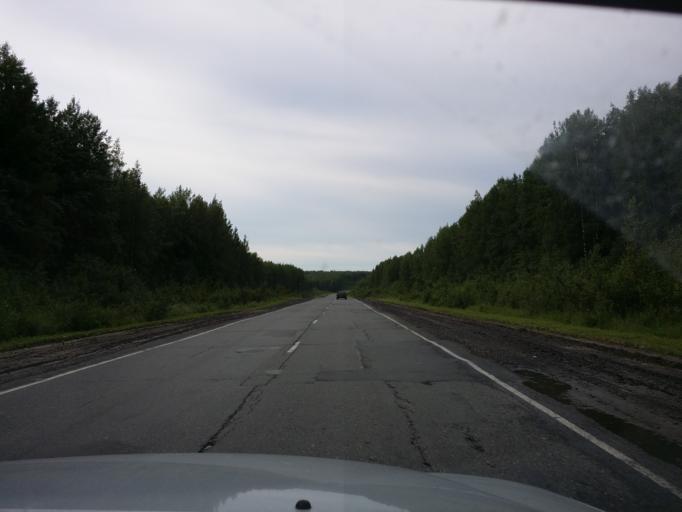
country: RU
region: Tjumen
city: Turtas
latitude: 58.7676
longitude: 68.9531
